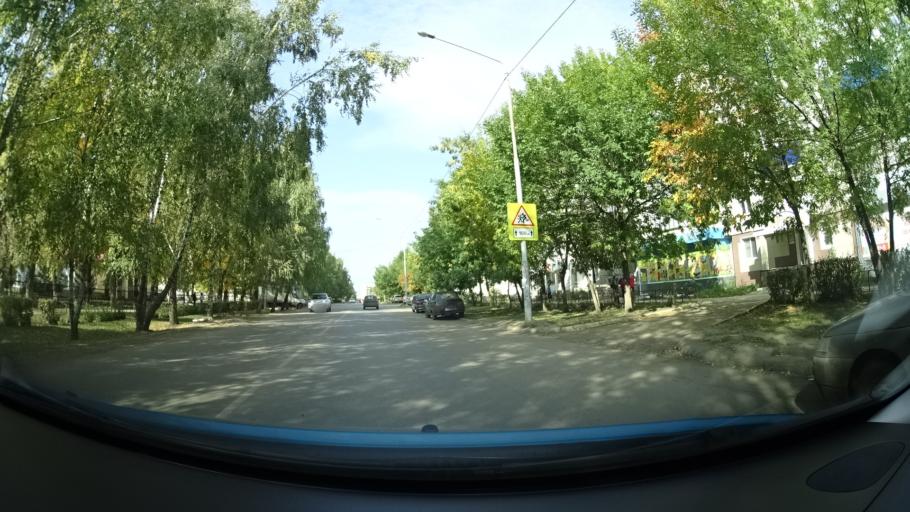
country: RU
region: Bashkortostan
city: Tuymazy
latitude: 54.6031
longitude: 53.6996
